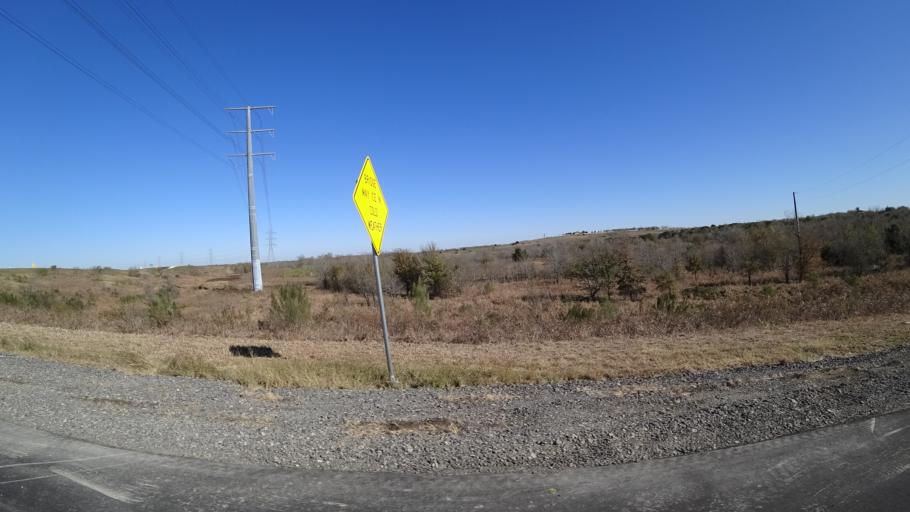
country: US
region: Texas
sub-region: Travis County
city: Garfield
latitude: 30.1165
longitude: -97.6584
